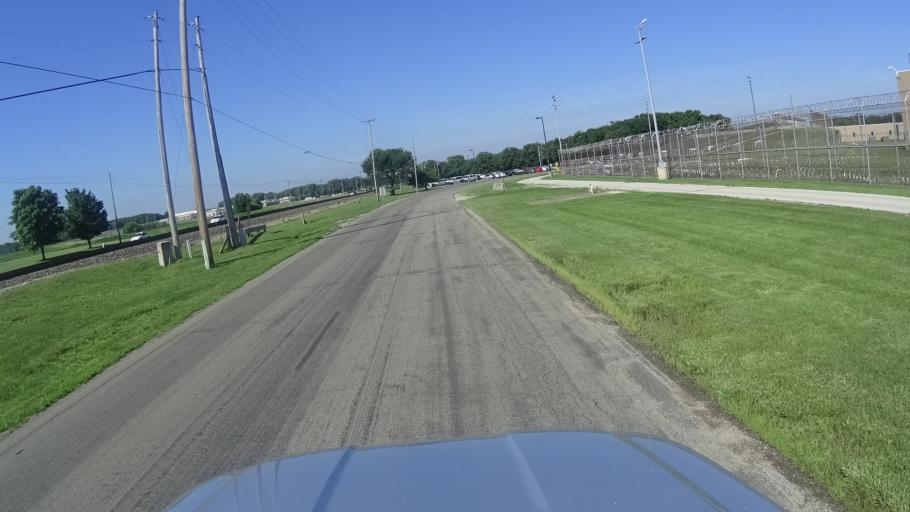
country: US
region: Indiana
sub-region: Madison County
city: Pendleton
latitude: 39.9743
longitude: -85.7704
